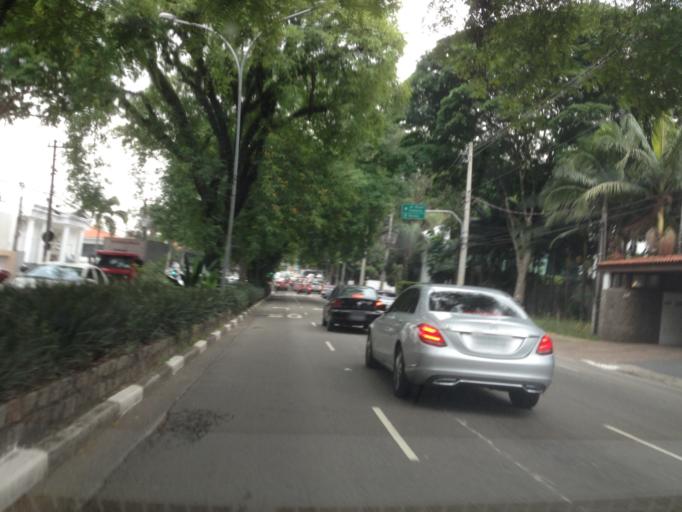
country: BR
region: Sao Paulo
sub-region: Sao Paulo
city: Sao Paulo
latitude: -23.5835
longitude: -46.6636
